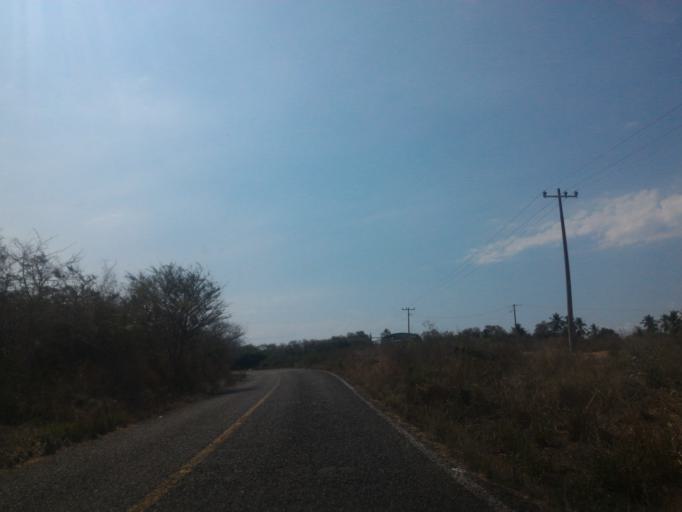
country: MX
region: Michoacan
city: Coahuayana Viejo
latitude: 18.3894
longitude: -103.5255
